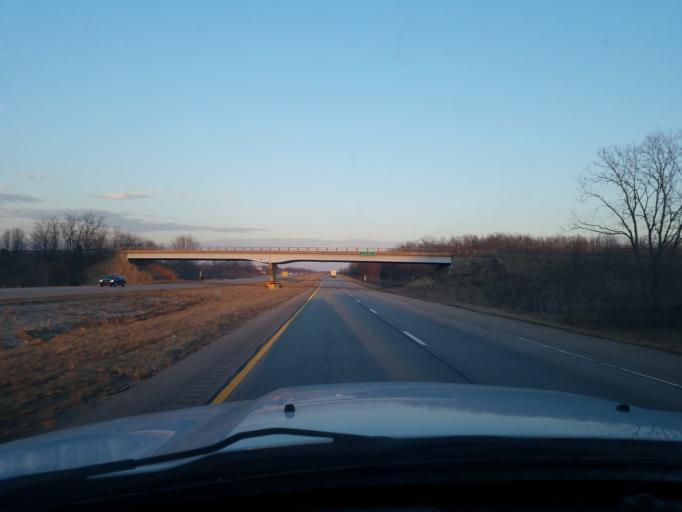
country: US
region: Indiana
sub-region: Warrick County
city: Chandler
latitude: 38.1870
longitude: -87.3561
